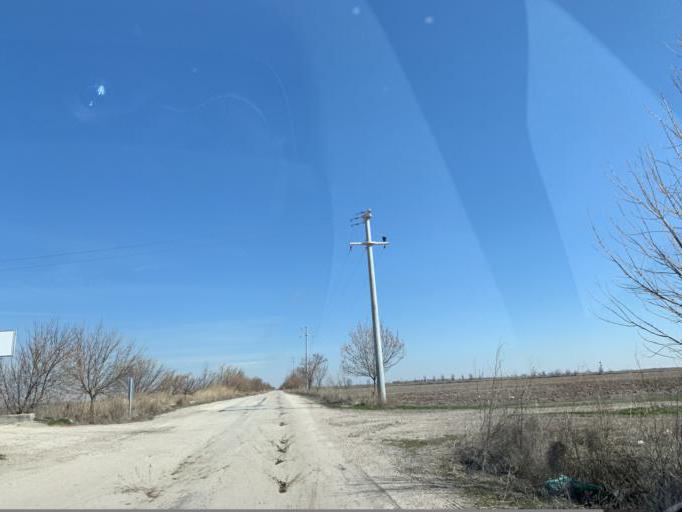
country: TR
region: Konya
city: Catalhoeyuek
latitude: 37.7420
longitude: 32.8013
